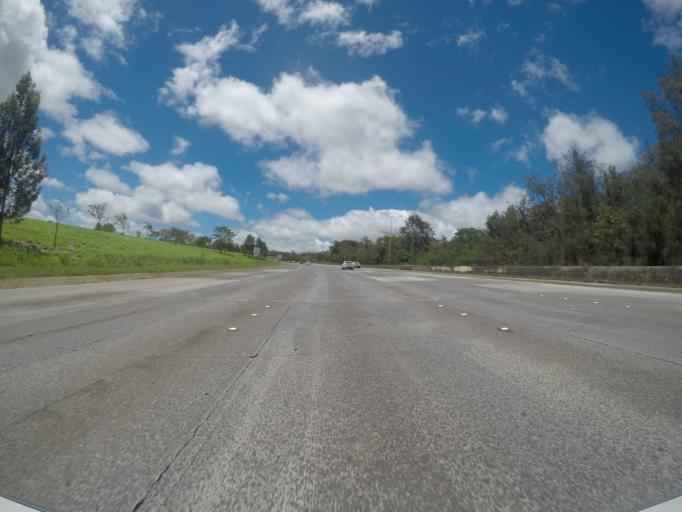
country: US
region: Hawaii
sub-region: Honolulu County
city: Mililani Town
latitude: 21.4365
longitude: -157.9943
